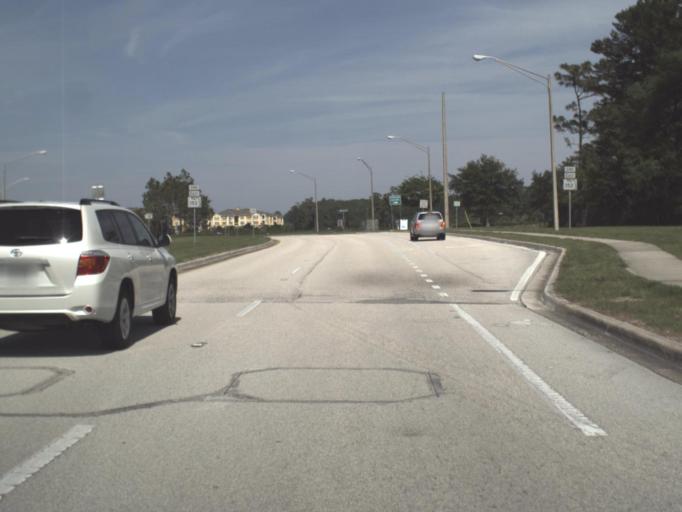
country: US
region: Florida
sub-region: Saint Johns County
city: Ponte Vedra Beach
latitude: 30.2159
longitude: -81.5127
